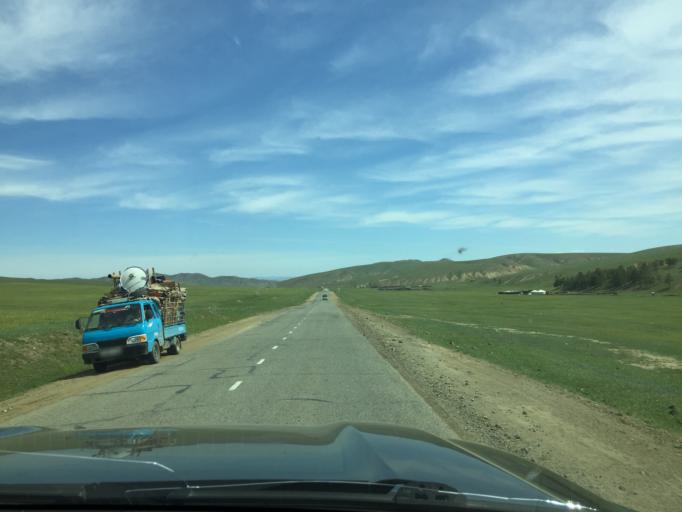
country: MN
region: Central Aimak
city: Javhlant
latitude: 48.6595
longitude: 106.1197
